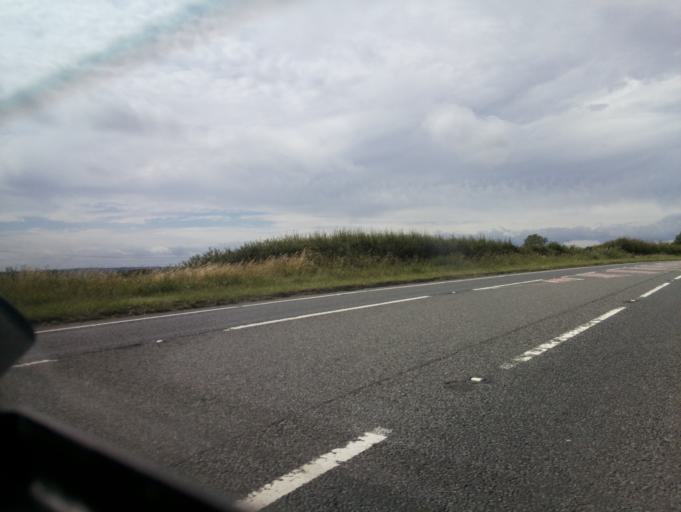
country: GB
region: England
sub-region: Dorset
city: Sherborne
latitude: 50.8040
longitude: -2.5514
